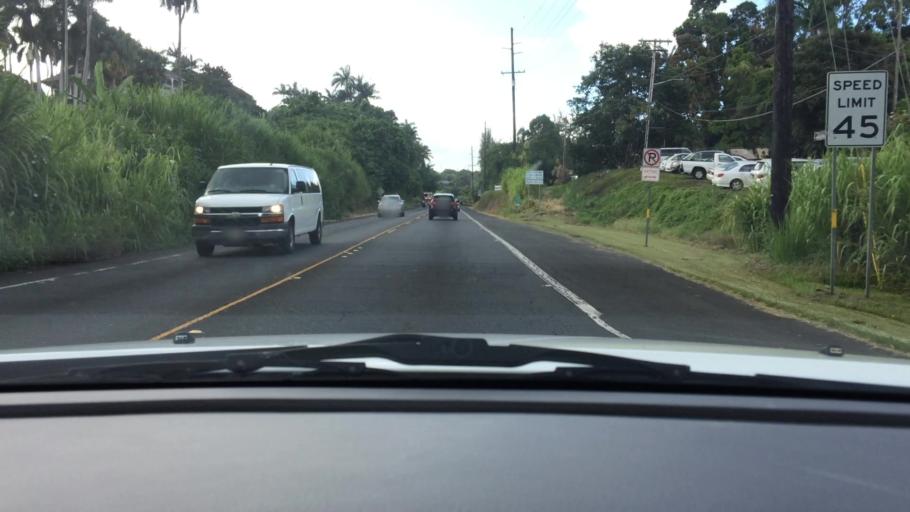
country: US
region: Hawaii
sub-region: Hawaii County
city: Hilo
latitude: 19.7307
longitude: -155.0890
